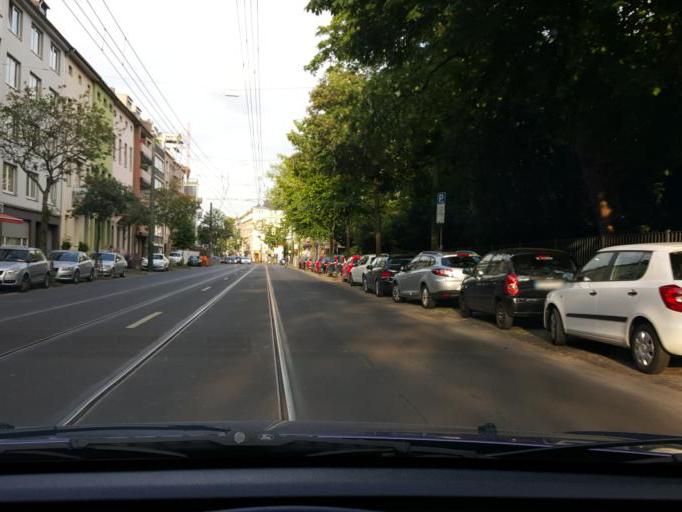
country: DE
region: North Rhine-Westphalia
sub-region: Regierungsbezirk Dusseldorf
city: Dusseldorf
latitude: 51.2107
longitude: 6.7721
